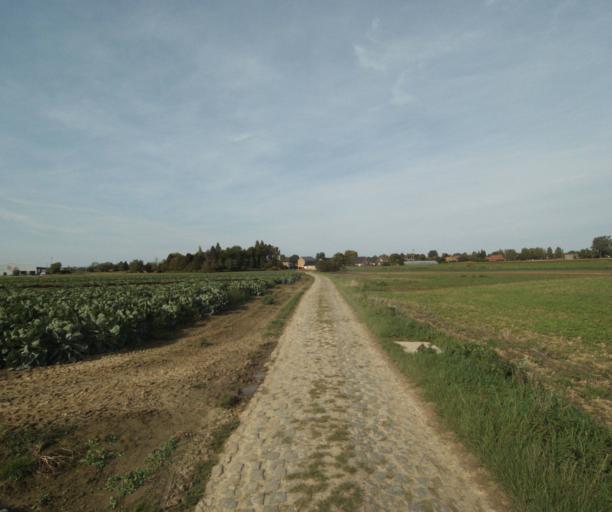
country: FR
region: Nord-Pas-de-Calais
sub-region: Departement du Nord
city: Radinghem-en-Weppes
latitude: 50.6103
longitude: 2.8857
